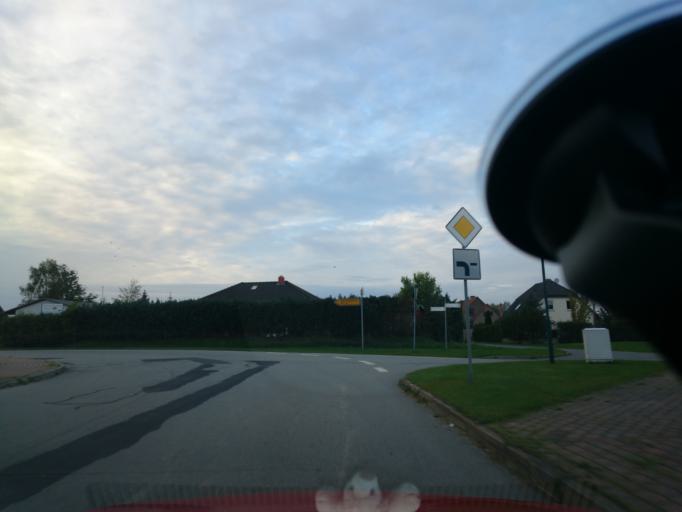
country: DE
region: Mecklenburg-Vorpommern
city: Saal
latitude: 54.3318
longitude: 12.5248
